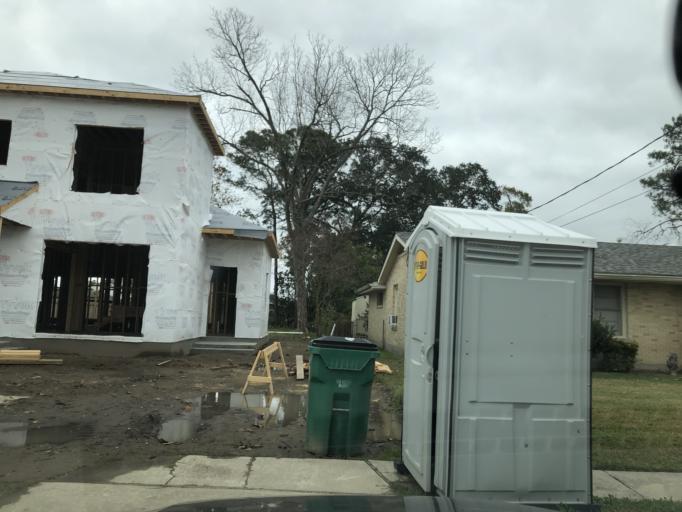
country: US
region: Louisiana
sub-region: Jefferson Parish
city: Metairie Terrace
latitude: 29.9838
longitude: -90.1662
